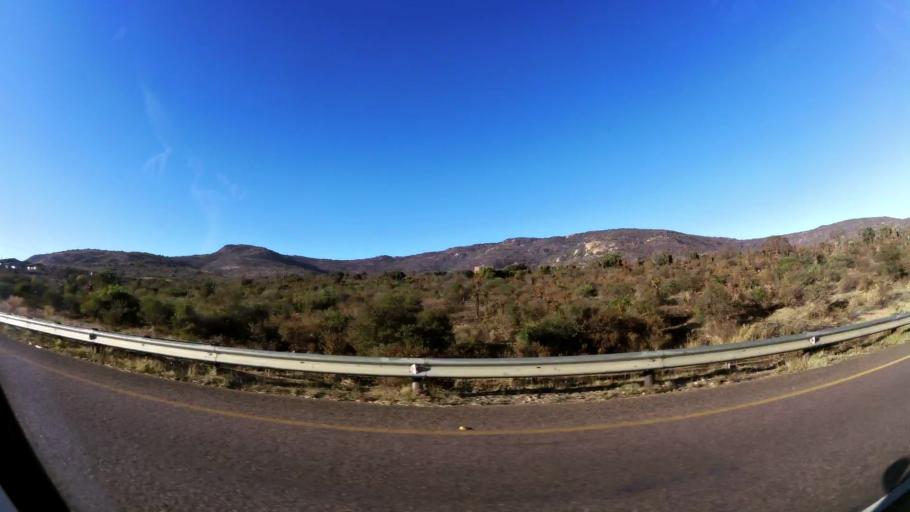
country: ZA
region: Limpopo
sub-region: Capricorn District Municipality
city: Mankoeng
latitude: -23.9303
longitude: 29.8536
